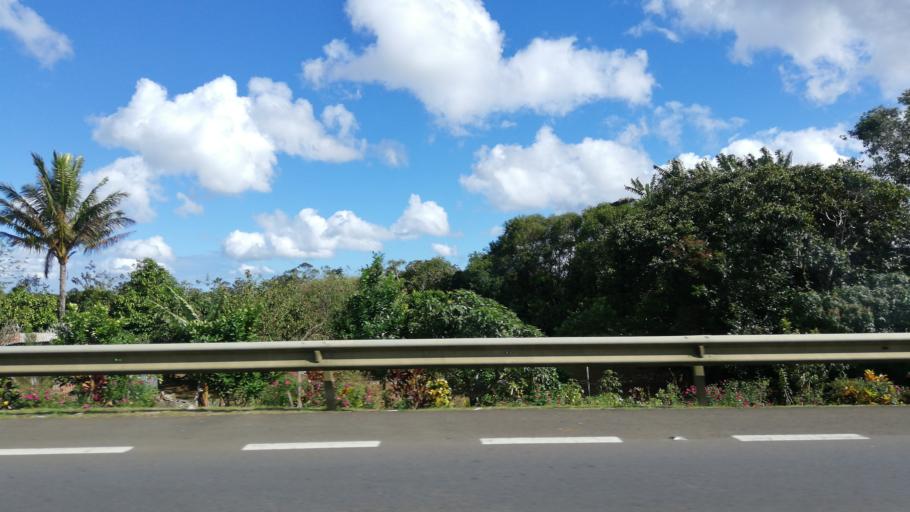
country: MU
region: Moka
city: La Dagotiere
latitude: -20.2539
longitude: 57.5640
